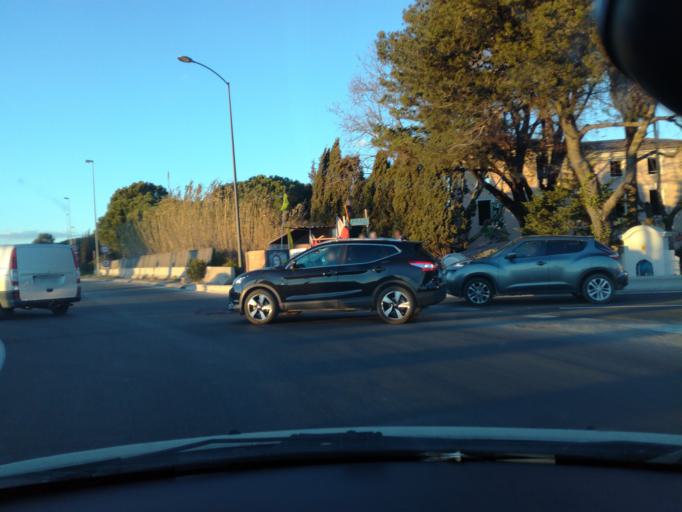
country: FR
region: Provence-Alpes-Cote d'Azur
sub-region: Departement du Var
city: Puget-sur-Argens
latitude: 43.4557
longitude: 6.6902
